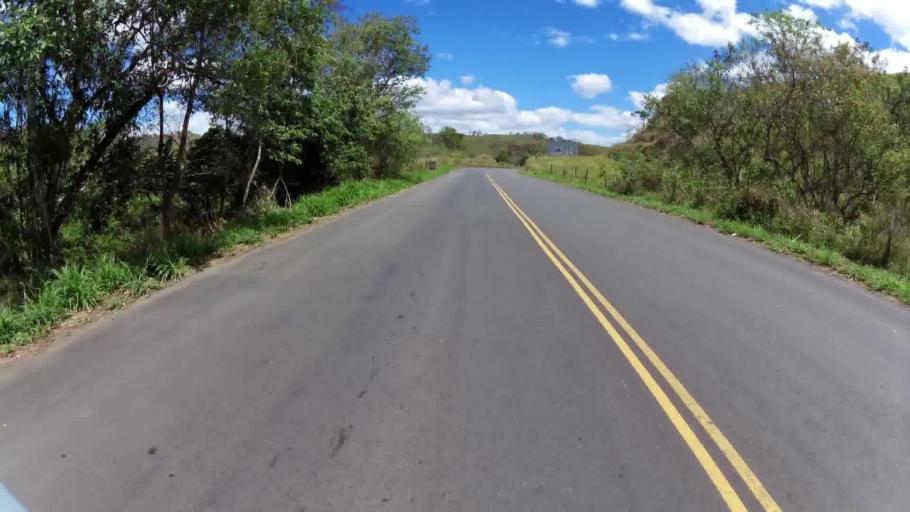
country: BR
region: Rio de Janeiro
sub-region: Itaperuna
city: Itaperuna
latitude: -21.3282
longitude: -41.8767
